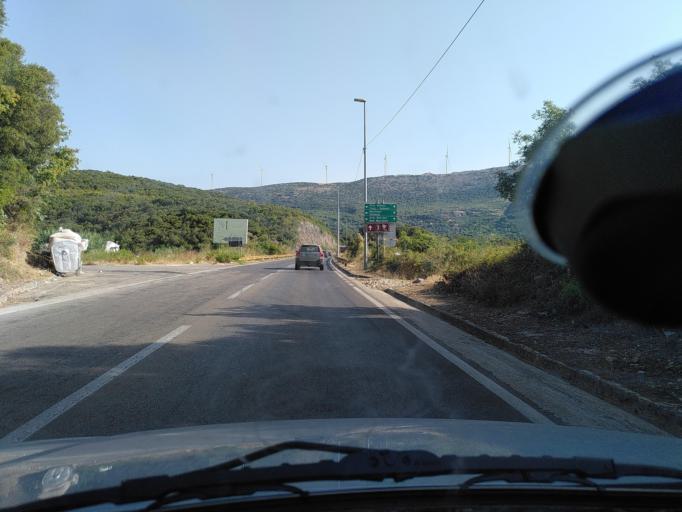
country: ME
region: Ulcinj
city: Ulcinj
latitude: 41.9583
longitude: 19.1908
